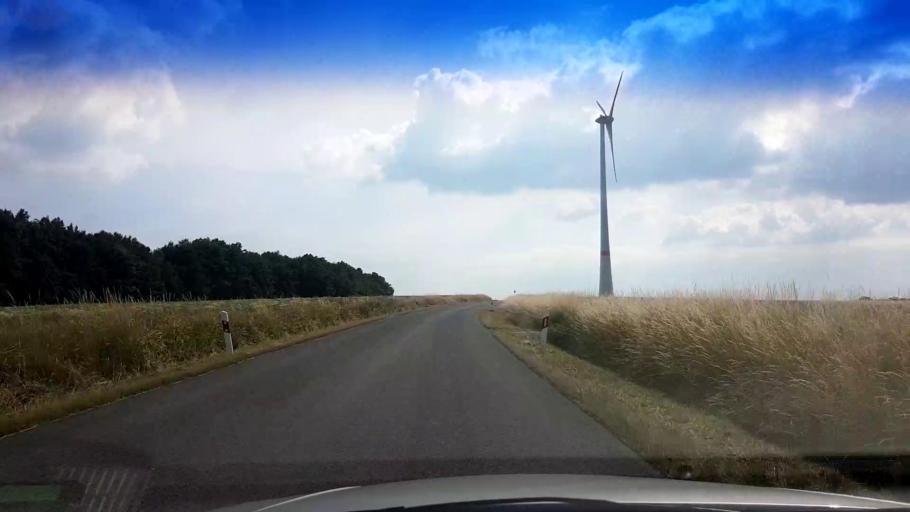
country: DE
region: Bavaria
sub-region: Upper Franconia
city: Priesendorf
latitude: 49.9130
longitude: 10.7405
